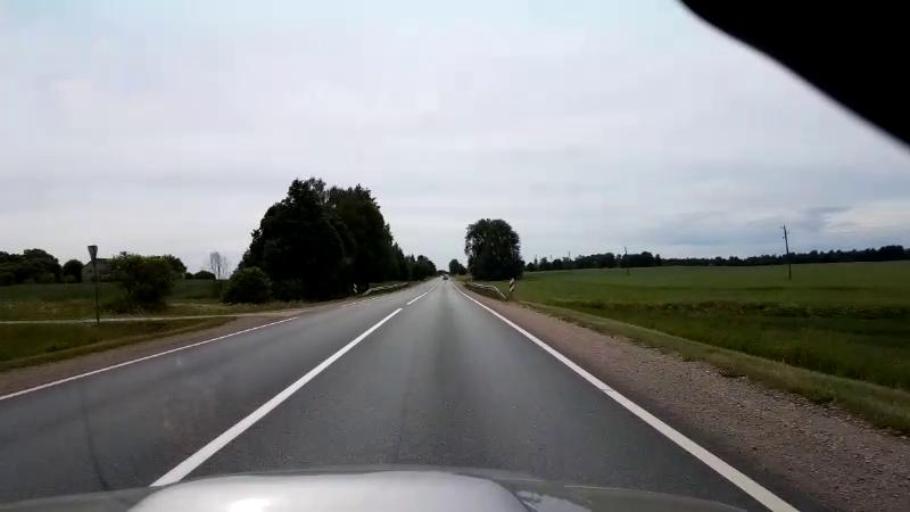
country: LV
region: Bauskas Rajons
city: Bauska
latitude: 56.4972
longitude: 24.1752
